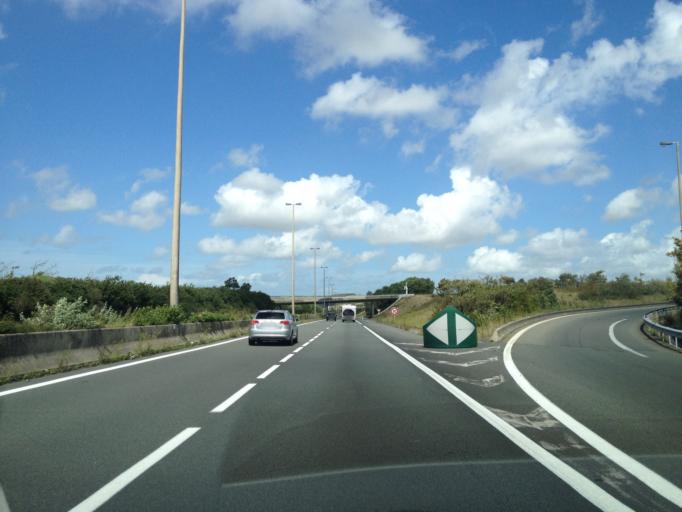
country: FR
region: Nord-Pas-de-Calais
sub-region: Departement du Pas-de-Calais
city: Marquise
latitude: 50.8250
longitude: 1.6996
